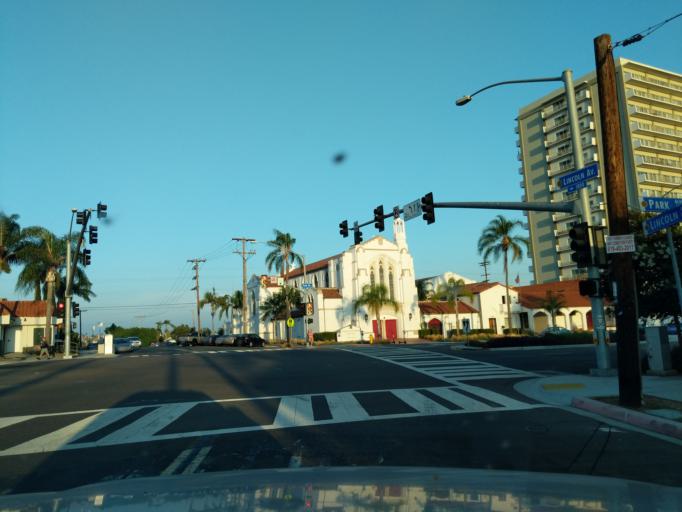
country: US
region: California
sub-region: San Diego County
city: San Diego
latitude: 32.7504
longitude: -117.1467
